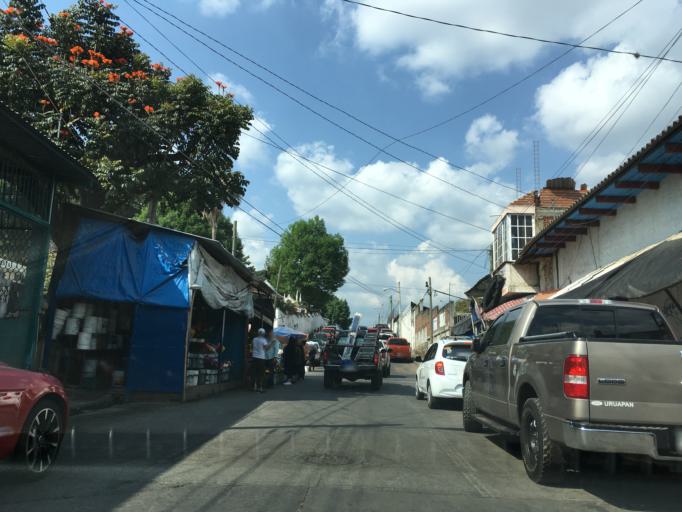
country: MX
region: Michoacan
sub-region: Uruapan
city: Uruapan
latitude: 19.4120
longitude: -102.0664
